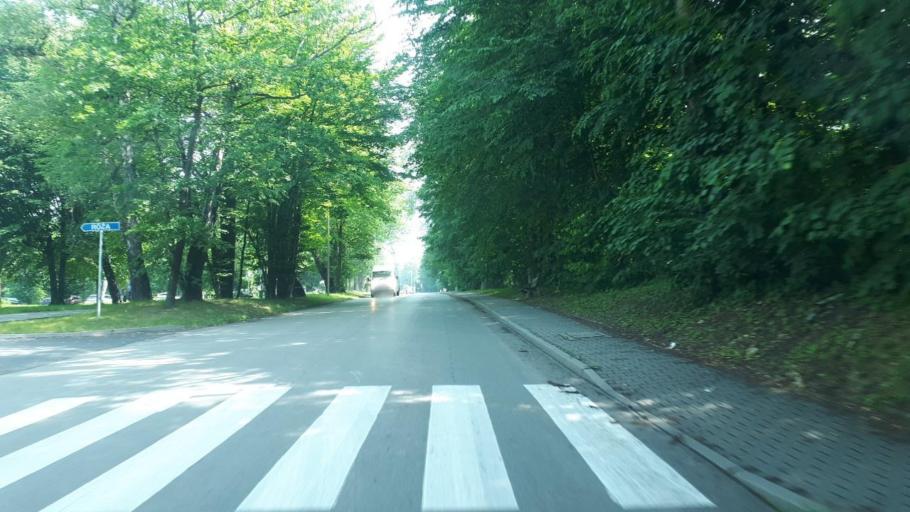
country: PL
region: Silesian Voivodeship
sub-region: Powiat cieszynski
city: Ustron
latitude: 49.7235
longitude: 18.8192
